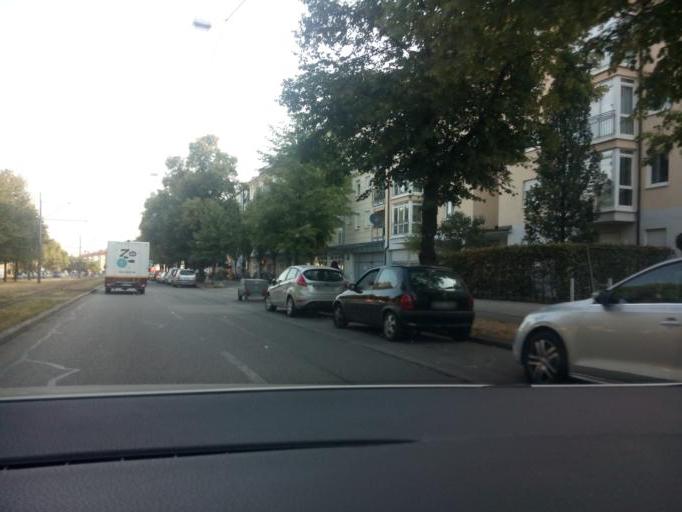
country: DE
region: Bavaria
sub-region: Upper Bavaria
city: Munich
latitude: 48.1033
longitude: 11.5971
